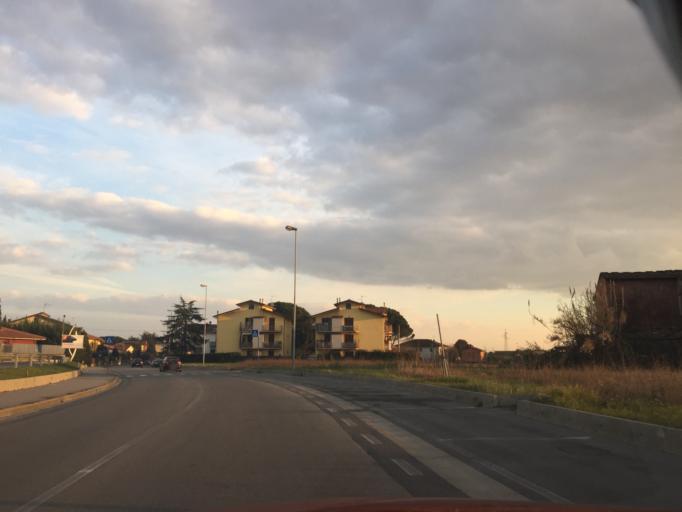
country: IT
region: Tuscany
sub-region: Provincia di Pistoia
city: Borgo a Buggiano
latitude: 43.8729
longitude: 10.7335
